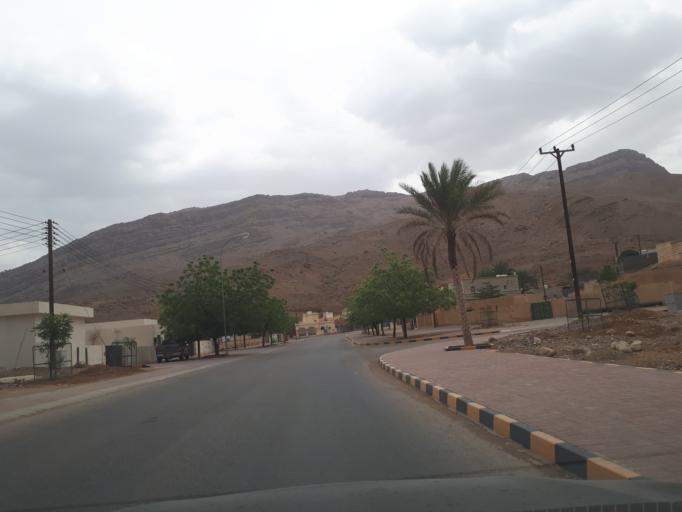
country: OM
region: Ash Sharqiyah
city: Badiyah
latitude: 22.5726
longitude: 59.0983
